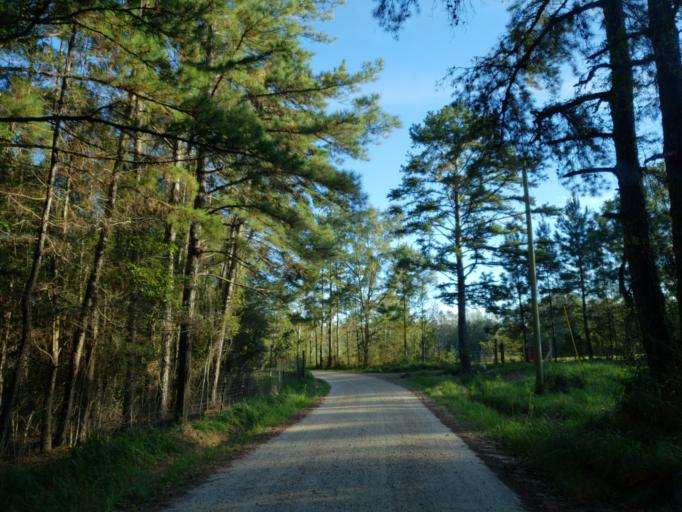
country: US
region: Mississippi
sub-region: Perry County
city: Richton
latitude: 31.3514
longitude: -88.8056
